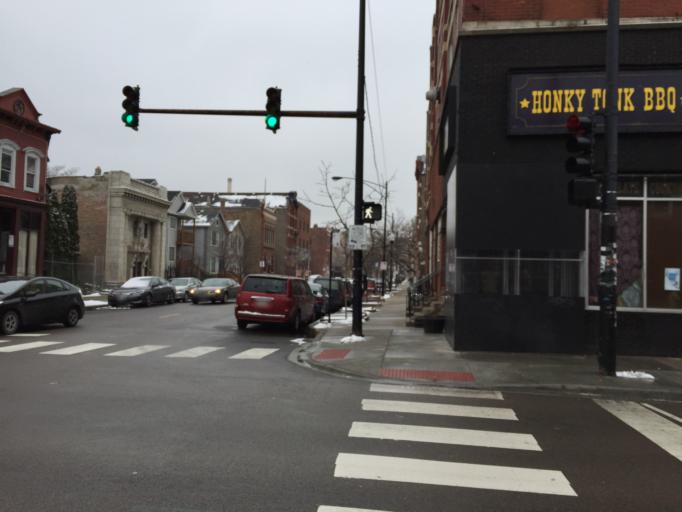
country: US
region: Illinois
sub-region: Cook County
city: Chicago
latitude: 41.8579
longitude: -87.6565
